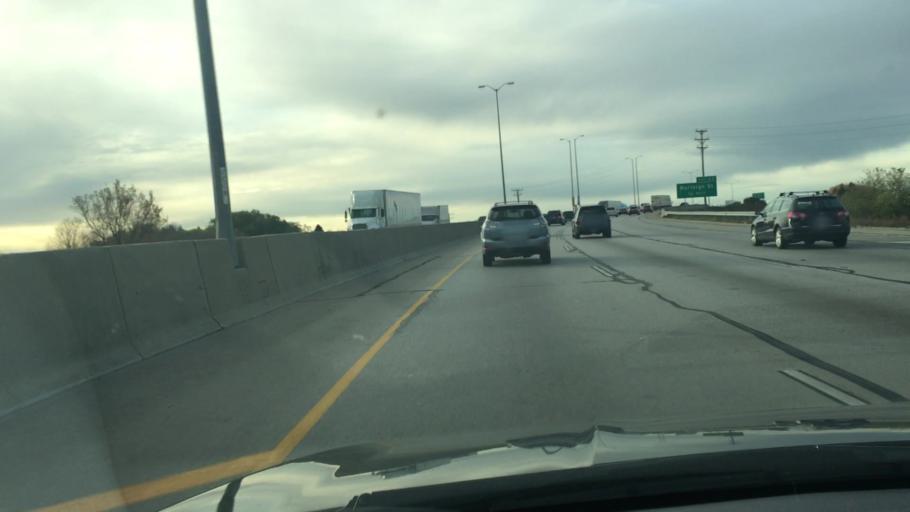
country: US
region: Wisconsin
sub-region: Waukesha County
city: Butler
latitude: 43.0848
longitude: -88.0572
